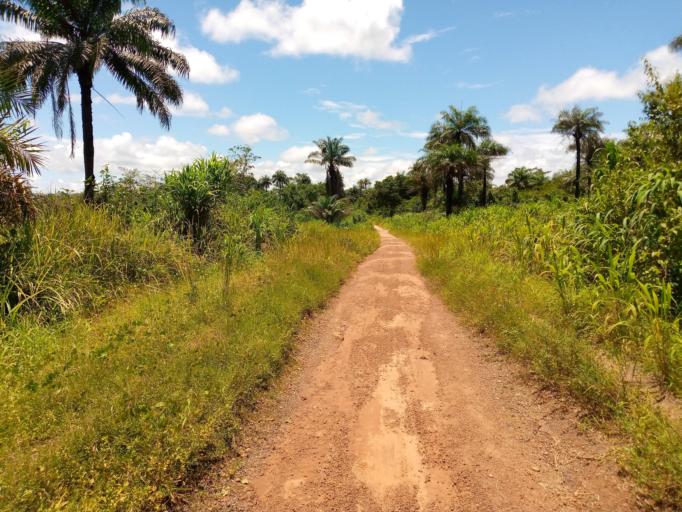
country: SL
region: Northern Province
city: Makeni
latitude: 9.0500
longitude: -12.1555
